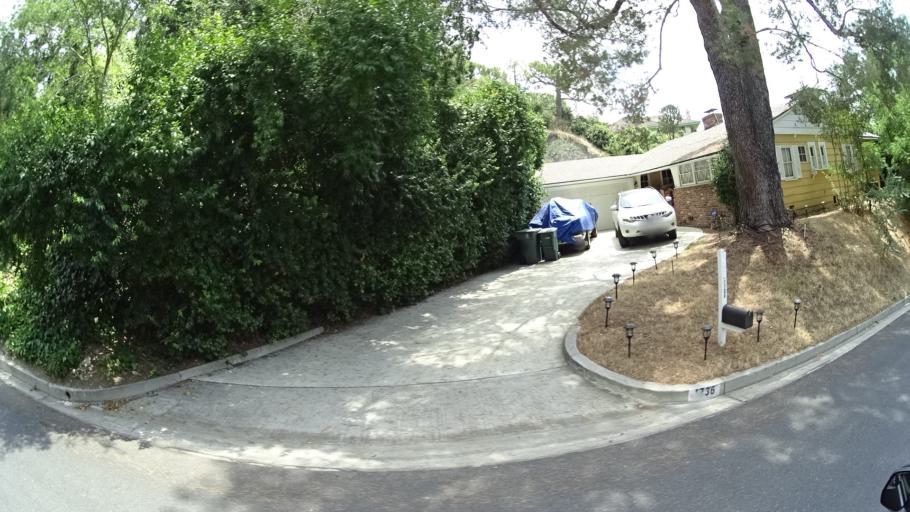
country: US
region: California
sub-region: Los Angeles County
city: Burbank
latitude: 34.1881
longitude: -118.2824
